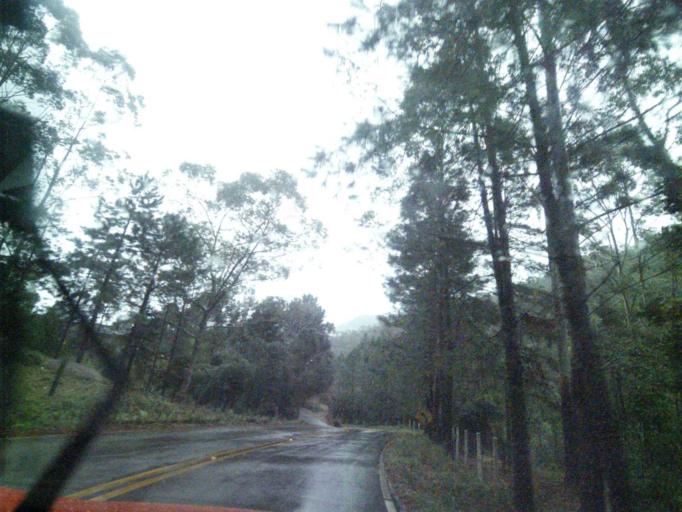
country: BR
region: Santa Catarina
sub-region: Anitapolis
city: Anitapolis
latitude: -27.7974
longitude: -49.0450
